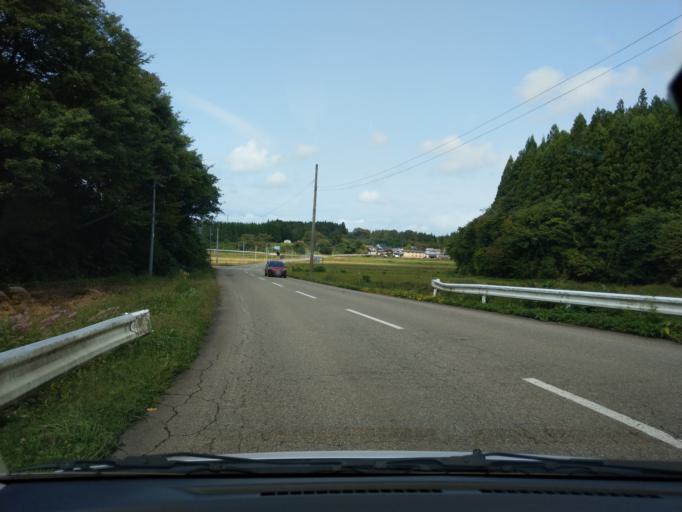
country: JP
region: Akita
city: Omagari
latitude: 39.5160
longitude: 140.3065
